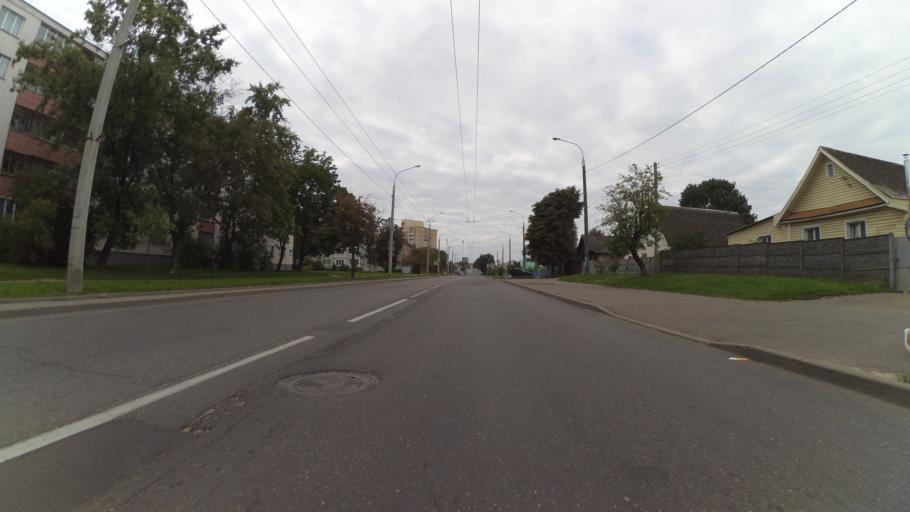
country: BY
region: Minsk
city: Vyaliki Trastsyanets
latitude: 53.8746
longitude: 27.6827
